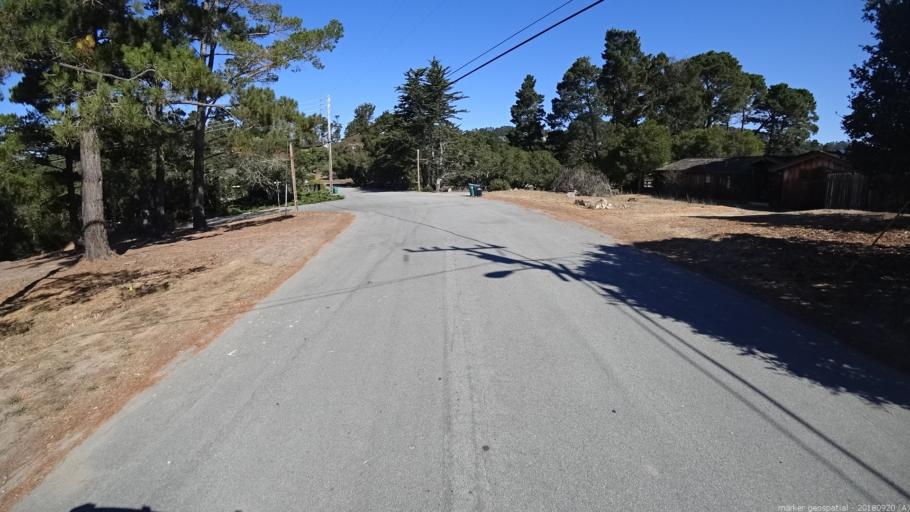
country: US
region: California
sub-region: Monterey County
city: Carmel-by-the-Sea
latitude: 36.5539
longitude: -121.8991
